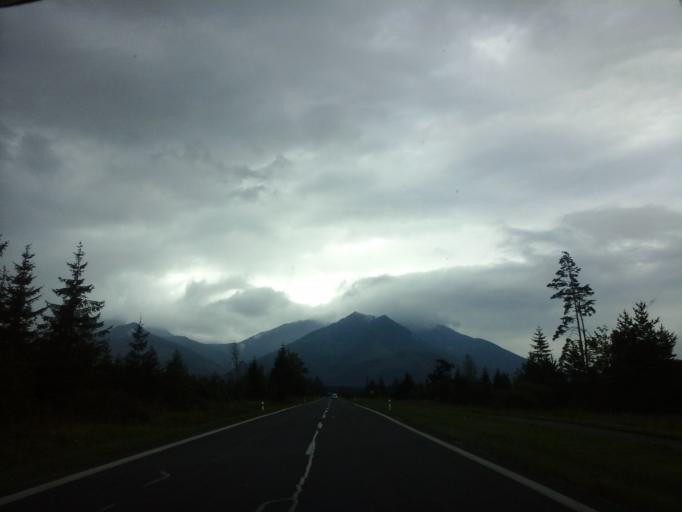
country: SK
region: Presovsky
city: Spisska Bela
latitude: 49.2116
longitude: 20.3651
